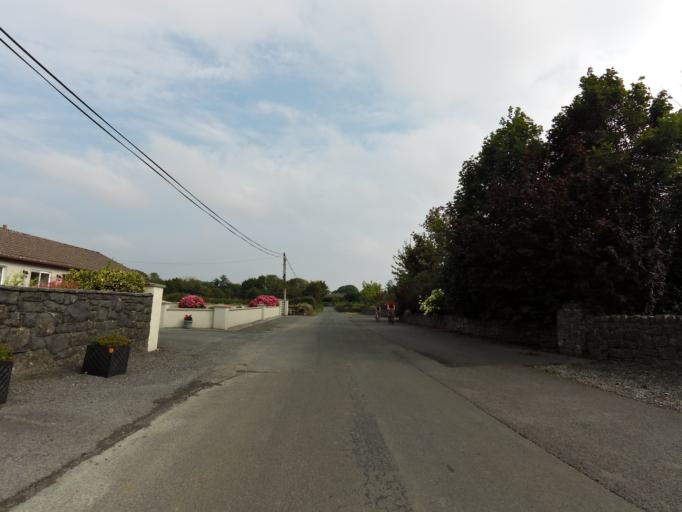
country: IE
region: Connaught
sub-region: County Galway
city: Gaillimh
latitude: 53.3038
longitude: -9.0711
